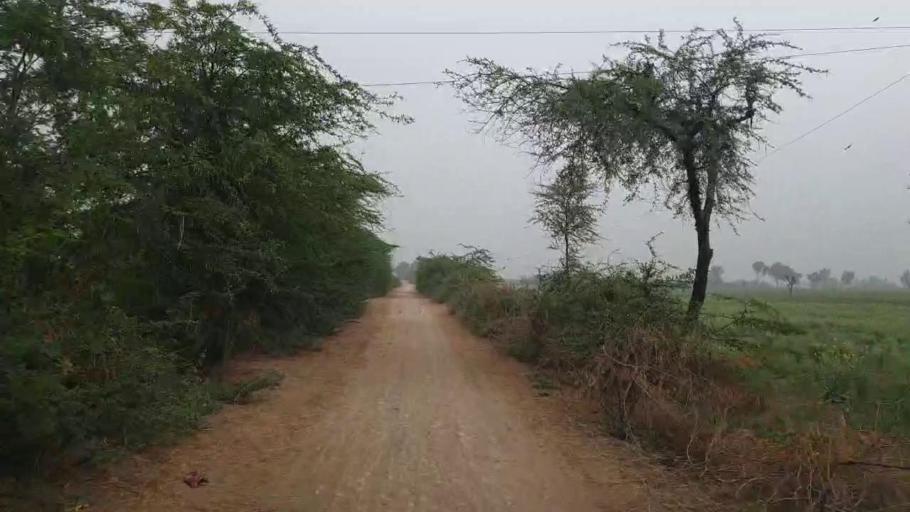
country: PK
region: Sindh
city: Badin
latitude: 24.6282
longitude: 68.7028
